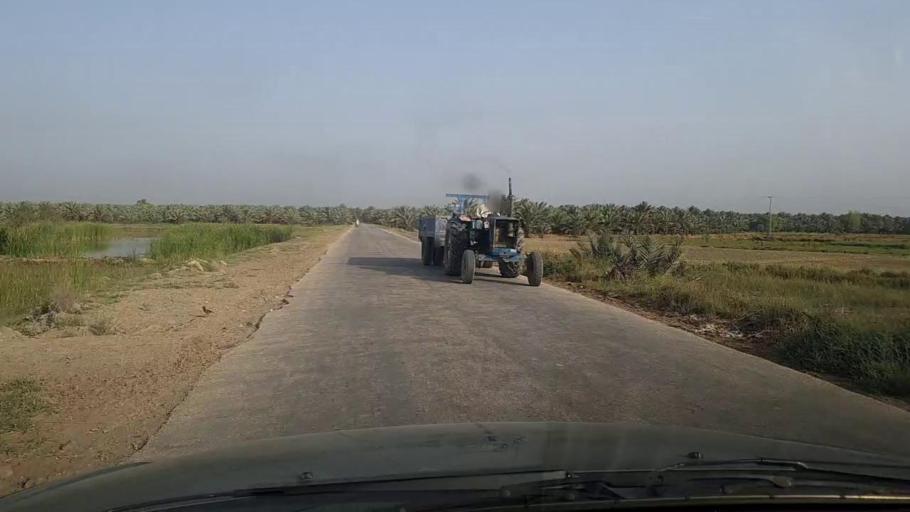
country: PK
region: Sindh
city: Pir jo Goth
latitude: 27.5656
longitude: 68.6436
